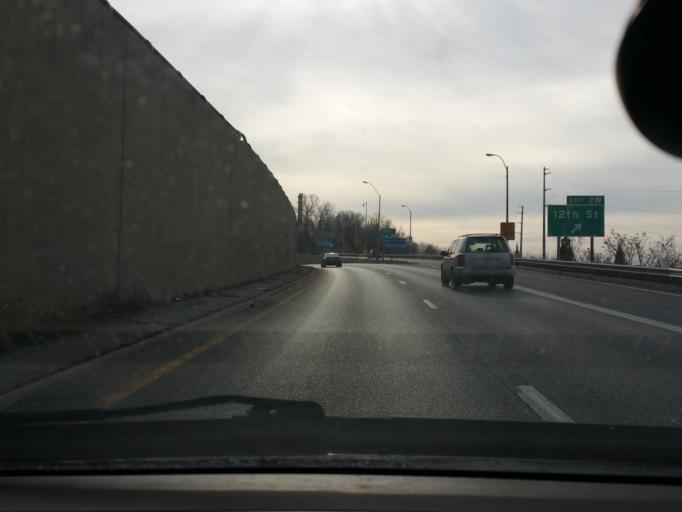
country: US
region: Missouri
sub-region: Jackson County
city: Kansas City
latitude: 39.1024
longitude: -94.5938
